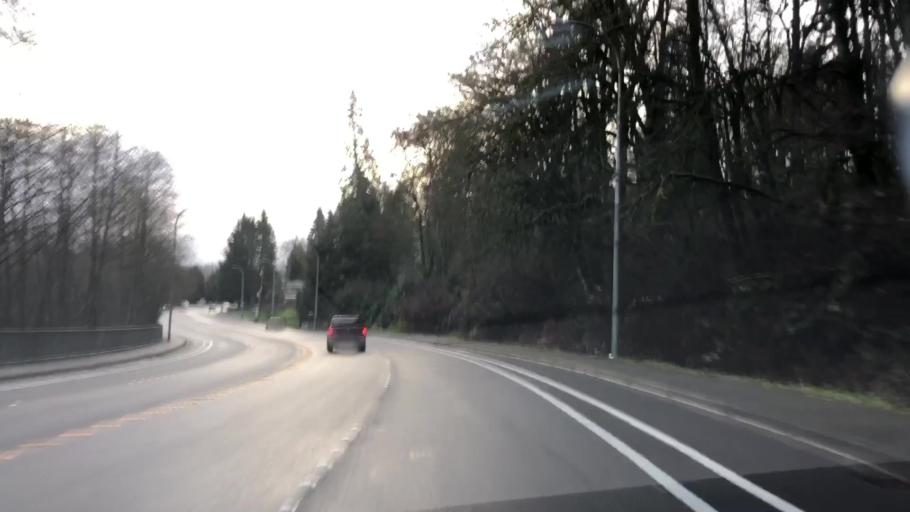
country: US
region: Washington
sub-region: King County
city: Newport
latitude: 47.5957
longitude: -122.1670
